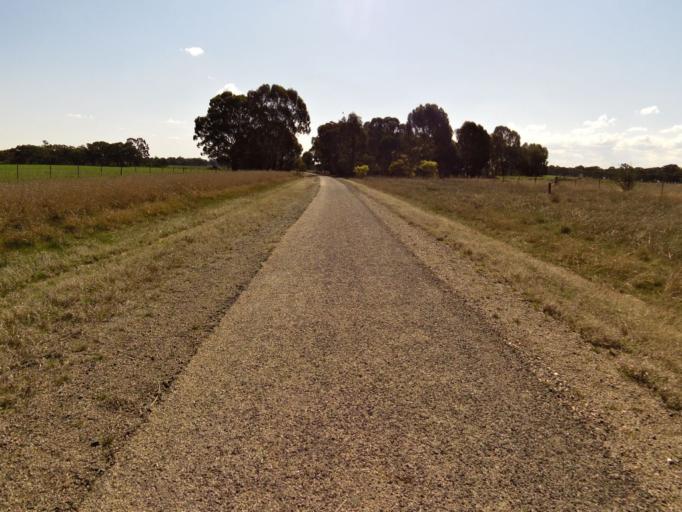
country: AU
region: New South Wales
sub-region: Corowa Shire
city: Corowa
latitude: -36.0384
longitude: 146.4526
